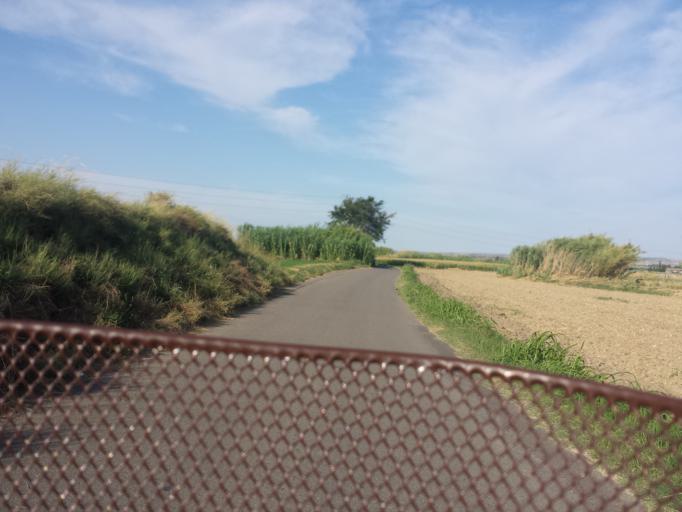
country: ES
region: Aragon
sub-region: Provincia de Zaragoza
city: Zaragoza
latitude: 41.6996
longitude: -0.8578
